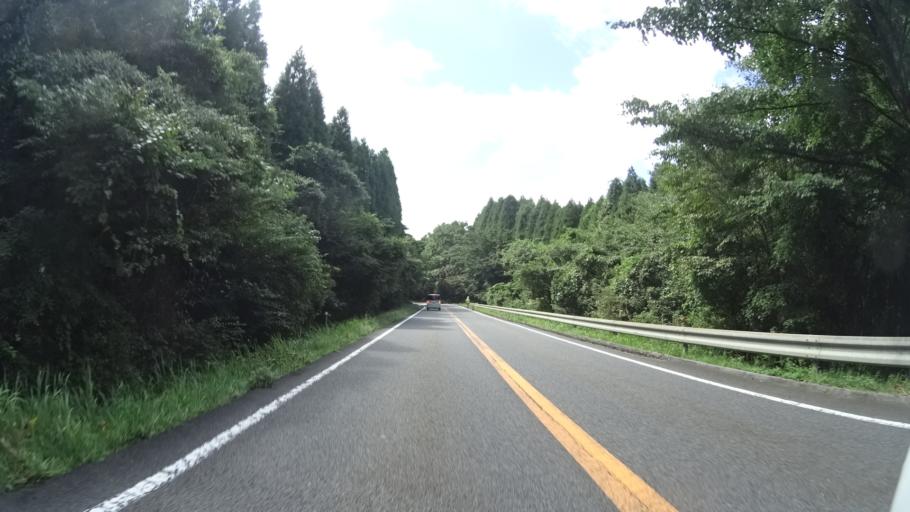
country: JP
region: Oita
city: Tsukawaki
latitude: 33.1952
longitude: 131.2502
